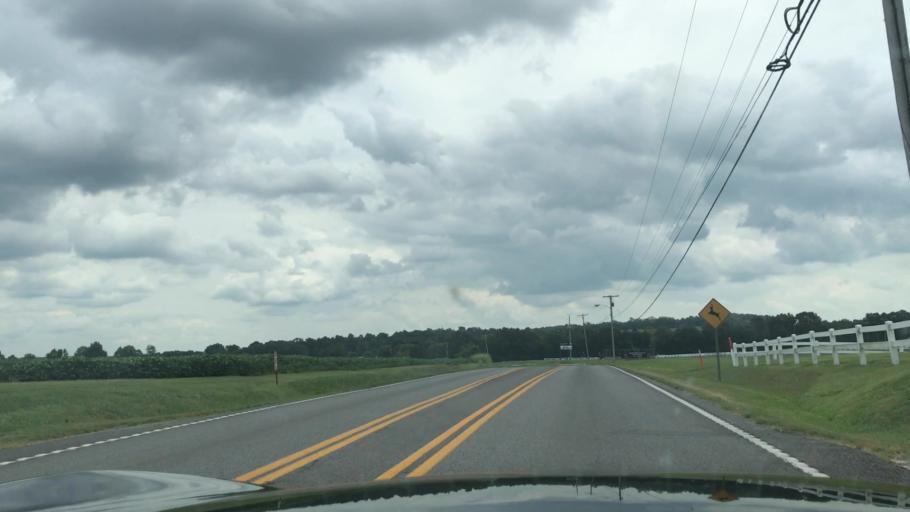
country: US
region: Kentucky
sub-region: Muhlenberg County
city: Greenville
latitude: 37.1987
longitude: -87.1317
